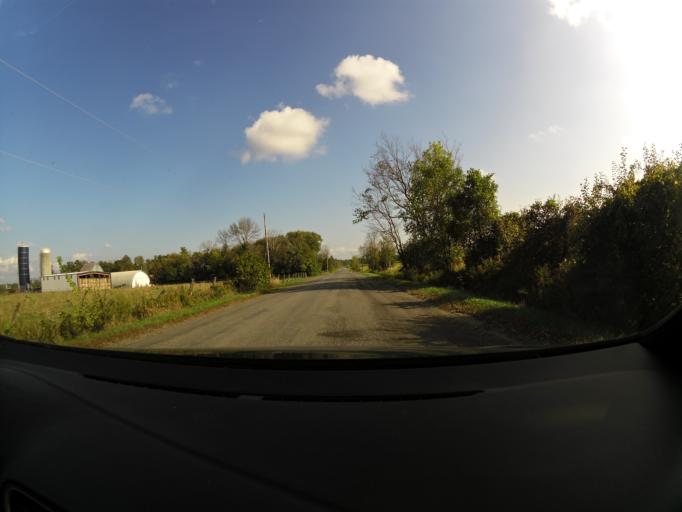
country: CA
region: Ontario
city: Arnprior
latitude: 45.4147
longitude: -76.2187
